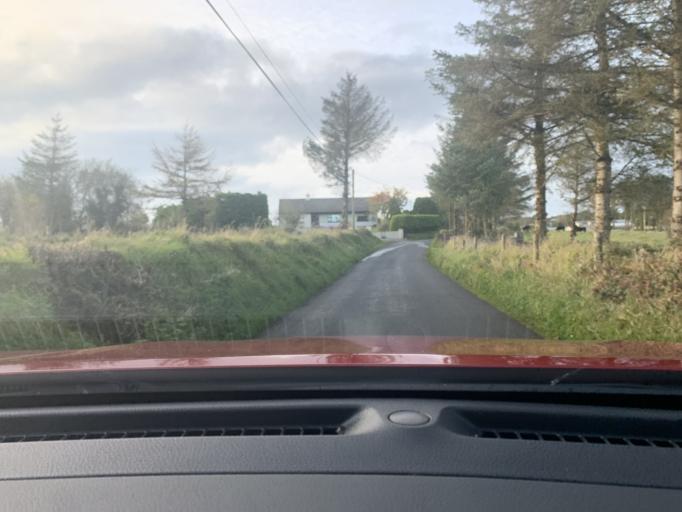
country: IE
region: Connaught
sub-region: Roscommon
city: Ballaghaderreen
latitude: 53.9147
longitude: -8.5894
